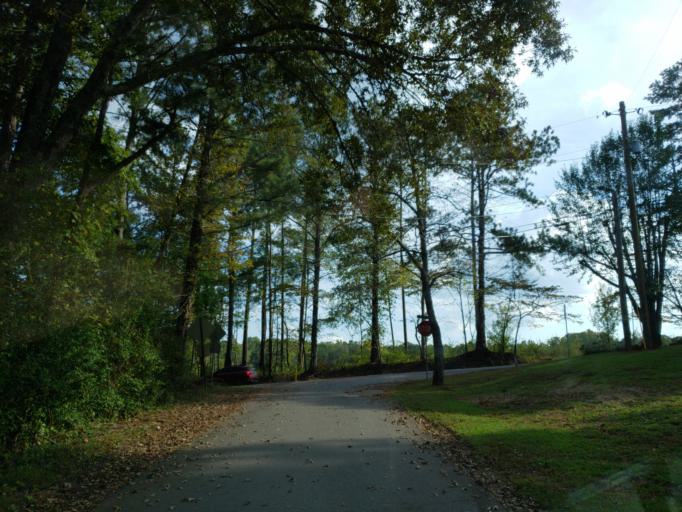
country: US
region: Georgia
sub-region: Fulton County
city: Roswell
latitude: 34.0853
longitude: -84.4216
